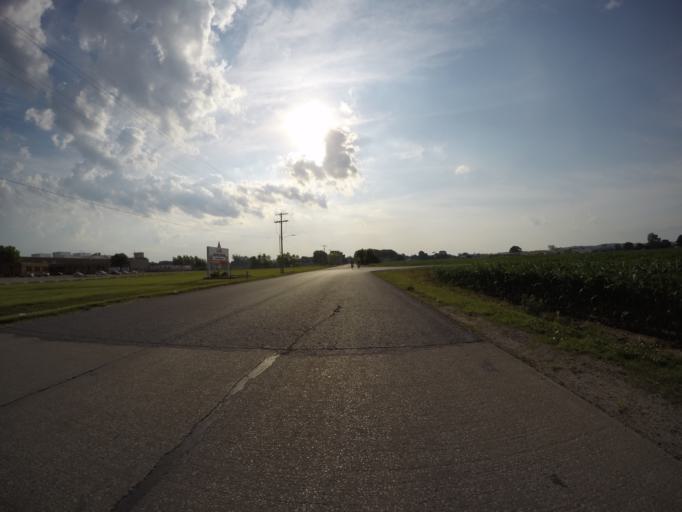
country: US
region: Kansas
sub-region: Doniphan County
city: Elwood
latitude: 39.7517
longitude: -94.8861
